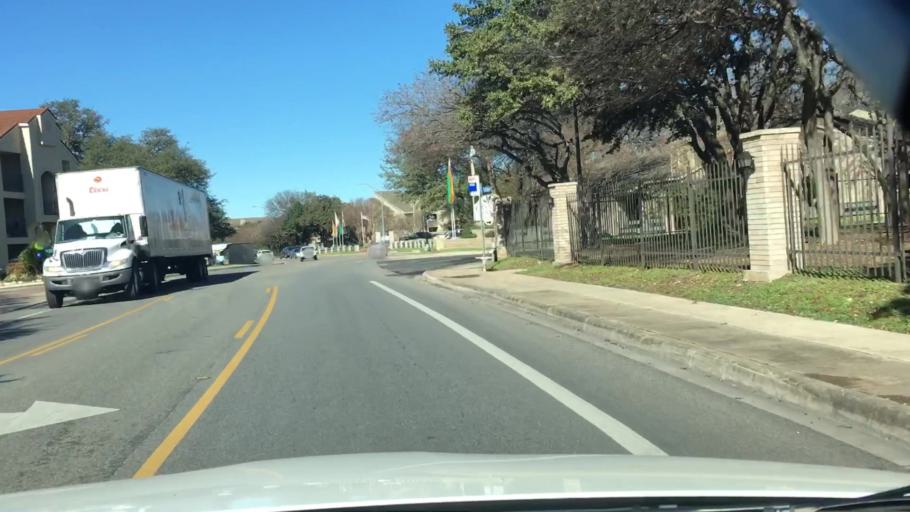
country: US
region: Texas
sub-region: Bexar County
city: Hollywood Park
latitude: 29.5906
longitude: -98.4487
